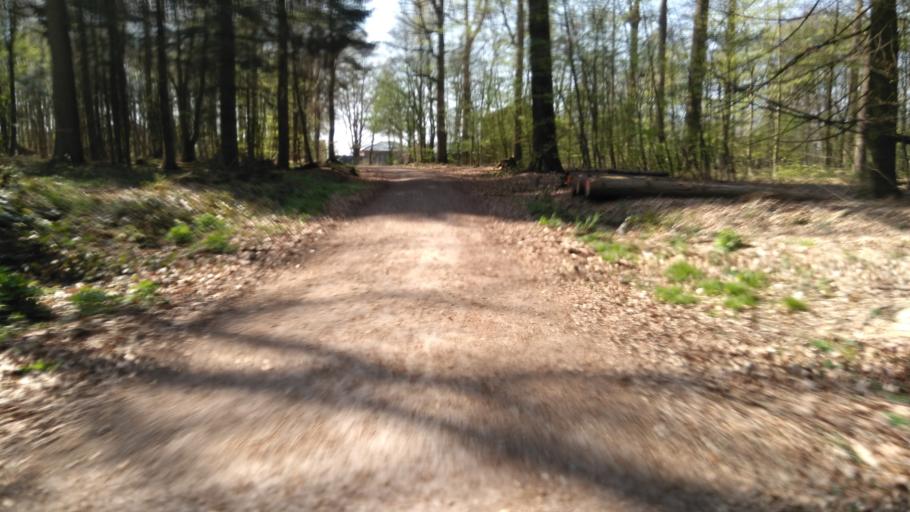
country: DE
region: Lower Saxony
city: Nottensdorf
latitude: 53.4781
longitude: 9.6231
